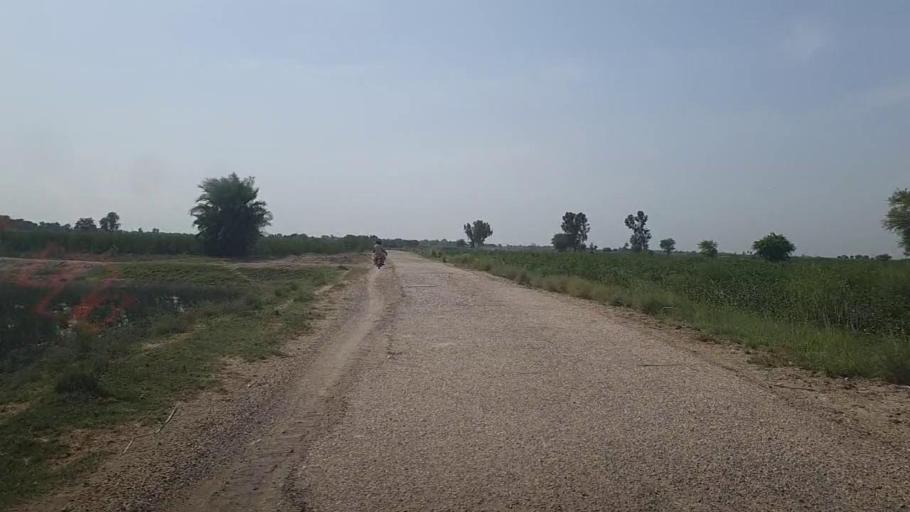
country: PK
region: Sindh
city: Ubauro
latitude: 28.1430
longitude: 69.8109
